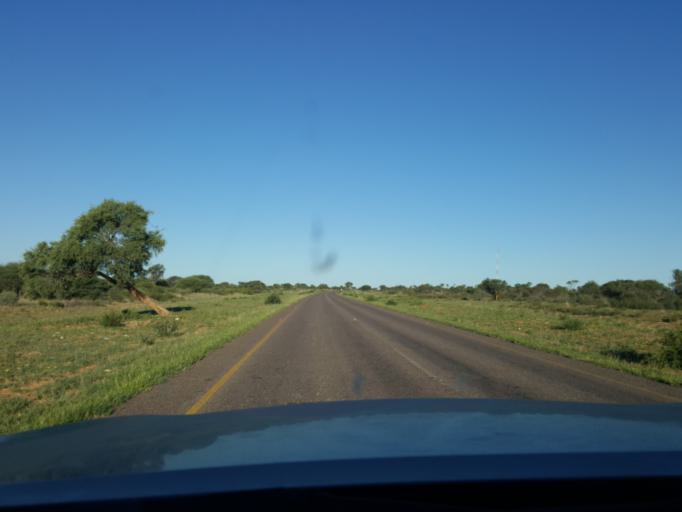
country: BW
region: Southern
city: Khakhea
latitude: -24.3030
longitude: 23.3967
